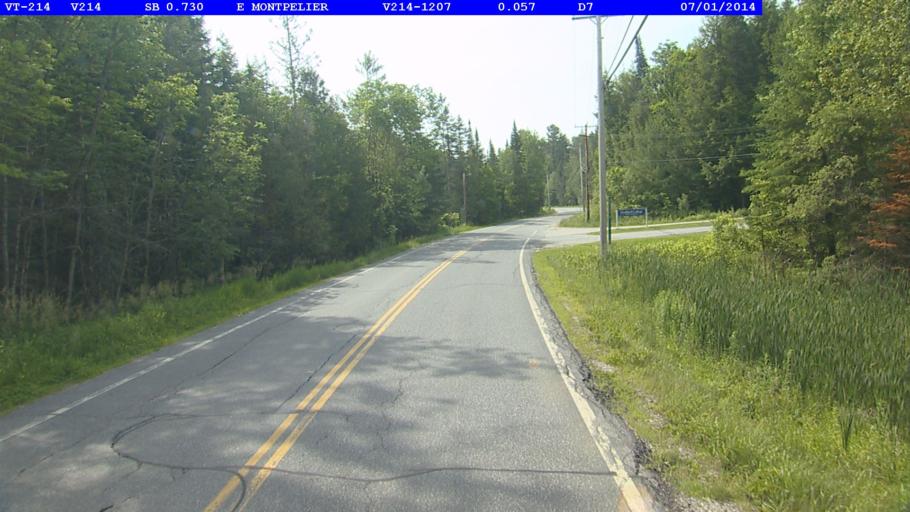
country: US
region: Vermont
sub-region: Washington County
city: Barre
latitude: 44.2870
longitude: -72.4408
